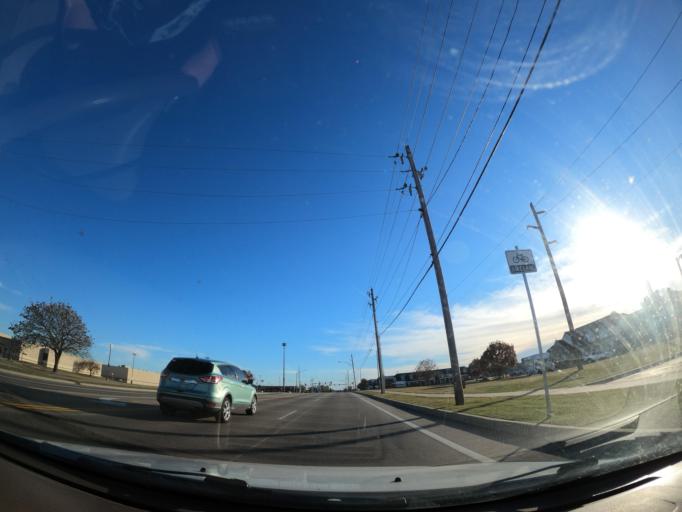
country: US
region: Oklahoma
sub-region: Tulsa County
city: Owasso
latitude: 36.2805
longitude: -95.8303
